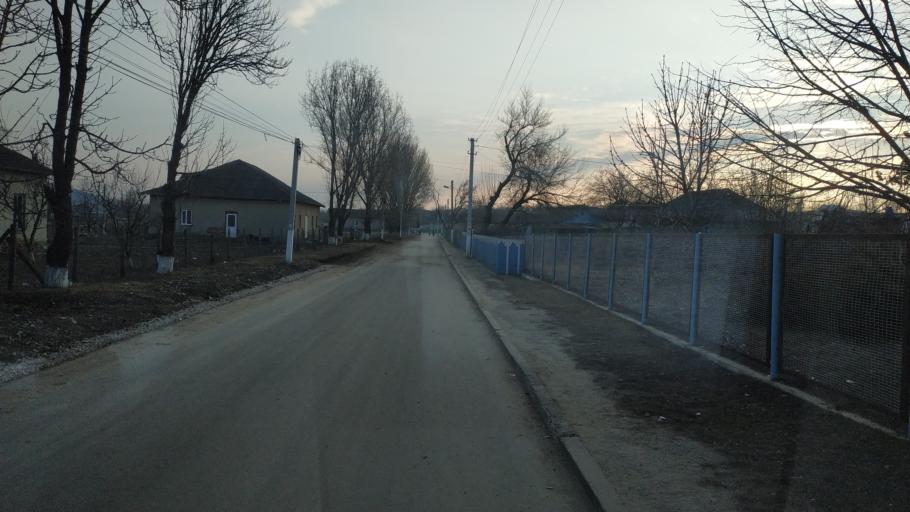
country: MD
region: Hincesti
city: Dancu
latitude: 46.7129
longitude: 28.3475
